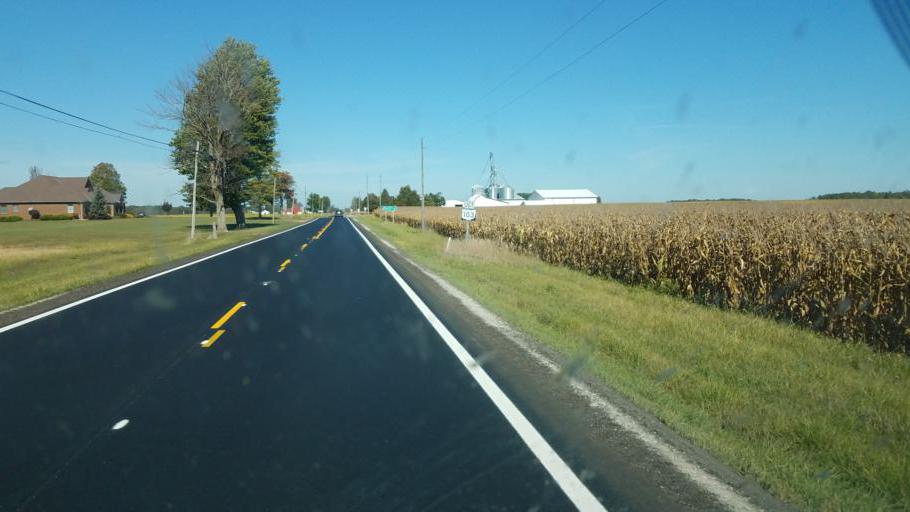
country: US
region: Ohio
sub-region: Crawford County
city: Bucyrus
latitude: 40.9484
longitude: -83.0163
